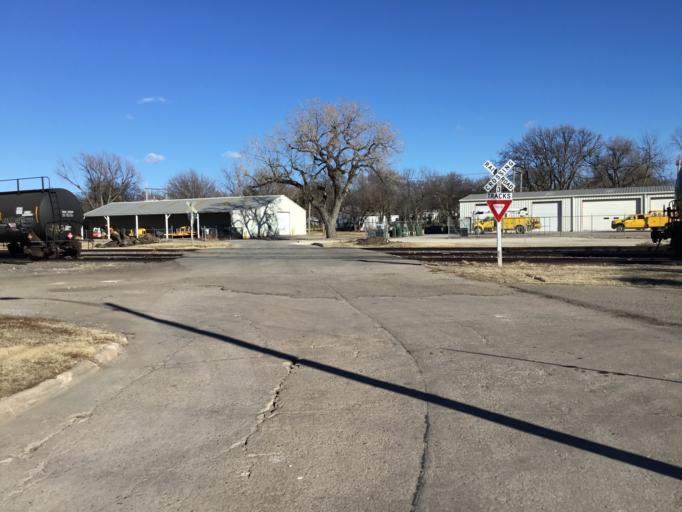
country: US
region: Kansas
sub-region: McPherson County
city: McPherson
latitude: 38.3658
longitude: -97.6727
